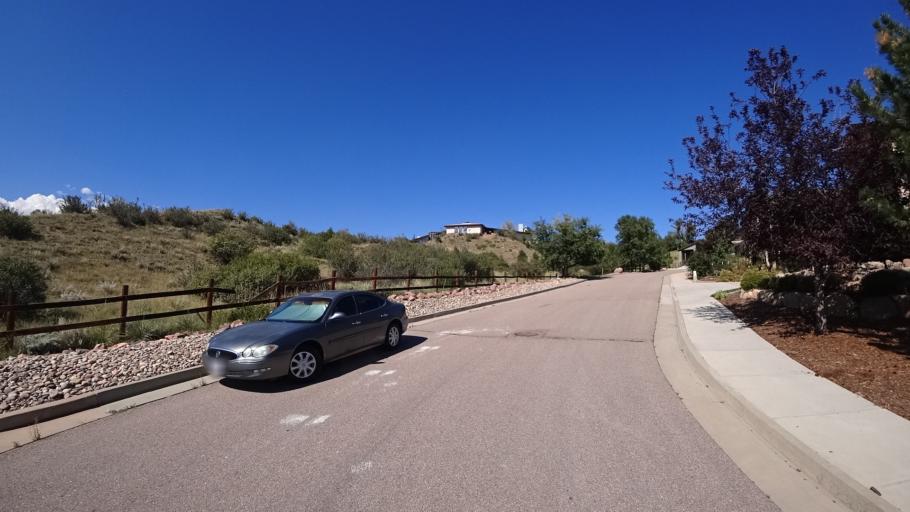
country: US
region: Colorado
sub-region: El Paso County
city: Colorado Springs
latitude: 38.8613
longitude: -104.8524
